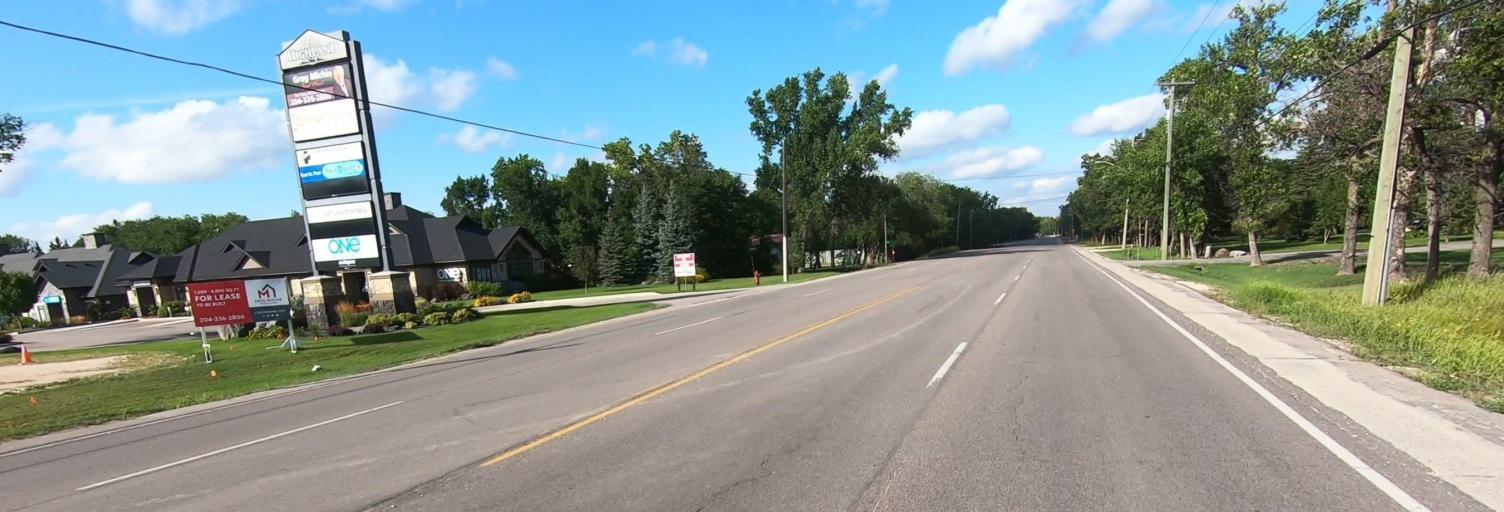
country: CA
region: Manitoba
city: Winnipeg
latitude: 49.9860
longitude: -97.0458
